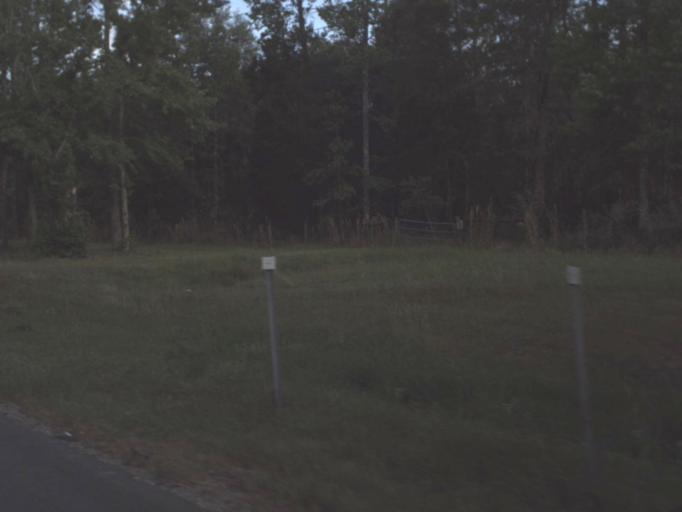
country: US
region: Florida
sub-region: Marion County
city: Silver Springs Shores
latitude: 29.2164
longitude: -81.9997
